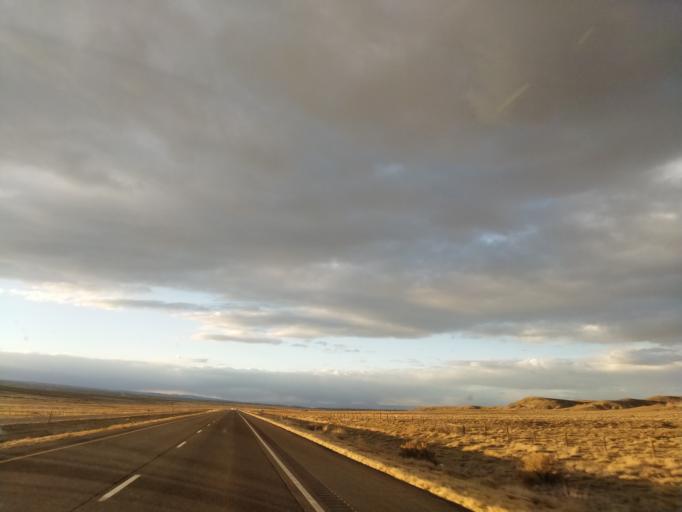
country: US
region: Colorado
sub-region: Mesa County
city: Palisade
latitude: 38.8758
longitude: -108.3435
